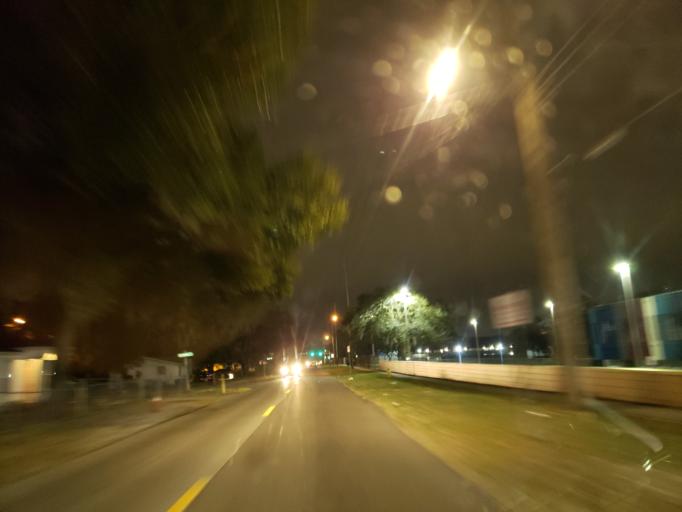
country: US
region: Florida
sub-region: Hillsborough County
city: University
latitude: 28.0300
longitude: -82.4347
